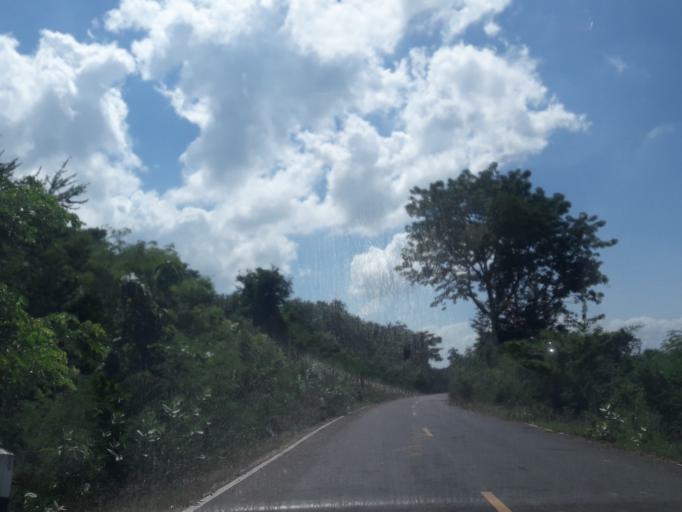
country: TH
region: Lop Buri
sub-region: Amphoe Tha Luang
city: Tha Luang
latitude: 15.0585
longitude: 101.0327
